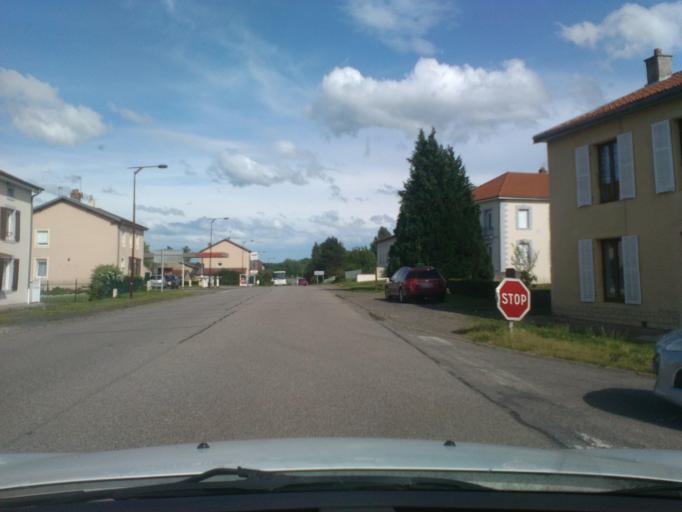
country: FR
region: Lorraine
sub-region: Departement de Meurthe-et-Moselle
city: Baccarat
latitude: 48.5498
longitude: 6.7239
